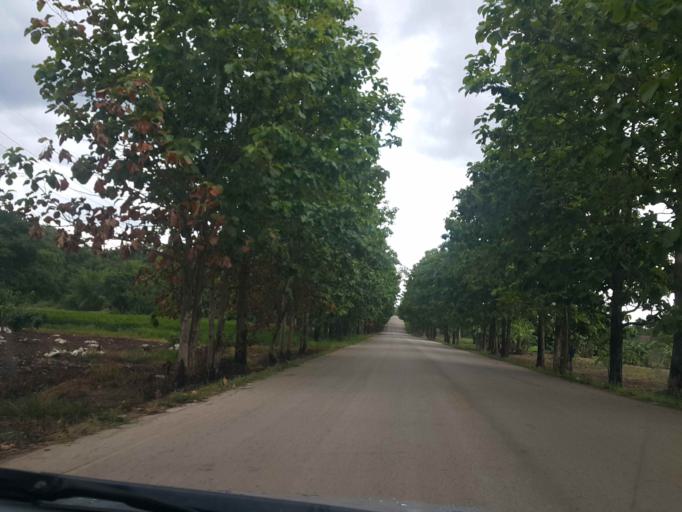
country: TH
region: Phayao
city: Dok Kham Tai
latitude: 18.9813
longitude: 100.0691
